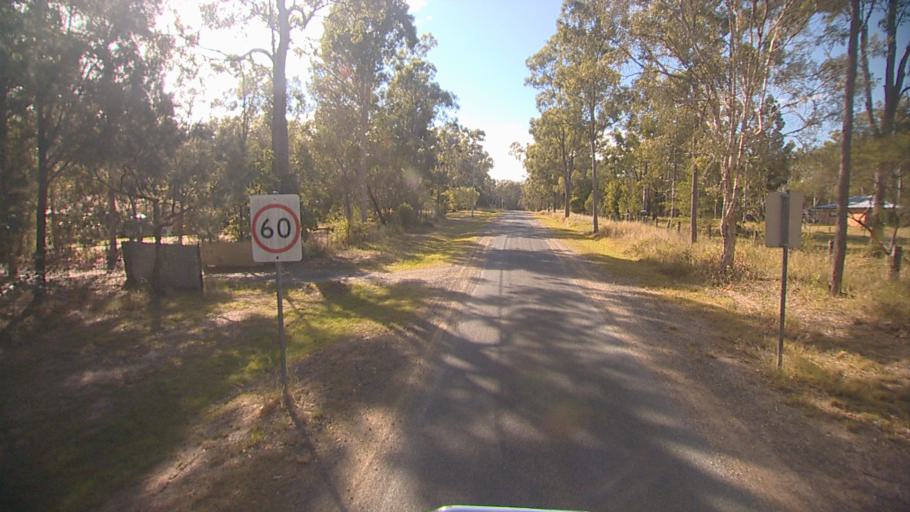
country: AU
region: Queensland
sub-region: Logan
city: Chambers Flat
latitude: -27.7849
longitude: 153.0719
